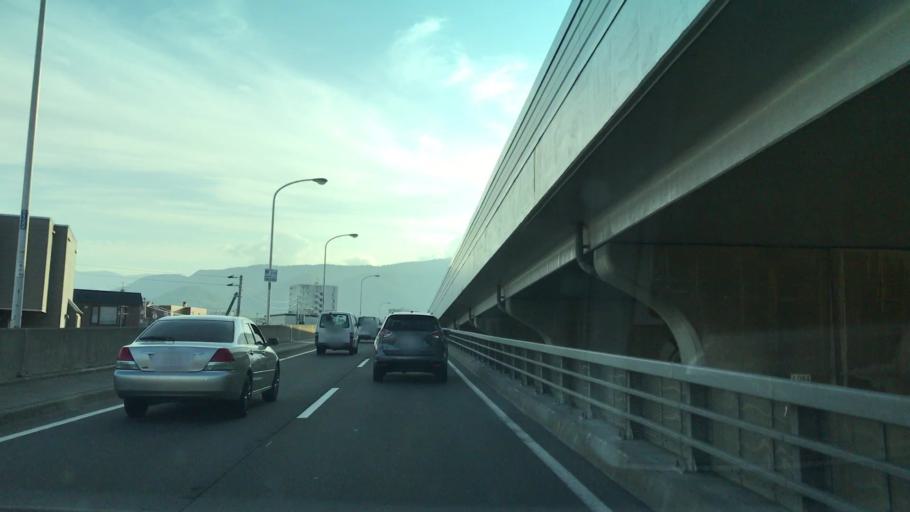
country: JP
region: Hokkaido
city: Sapporo
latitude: 43.0947
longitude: 141.2899
